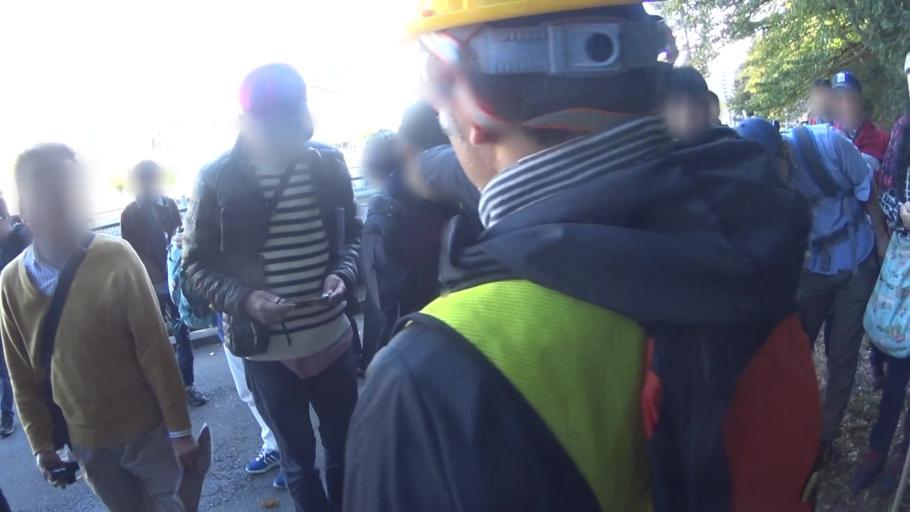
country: JP
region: Tokyo
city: Chofugaoka
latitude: 35.6058
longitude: 139.4980
